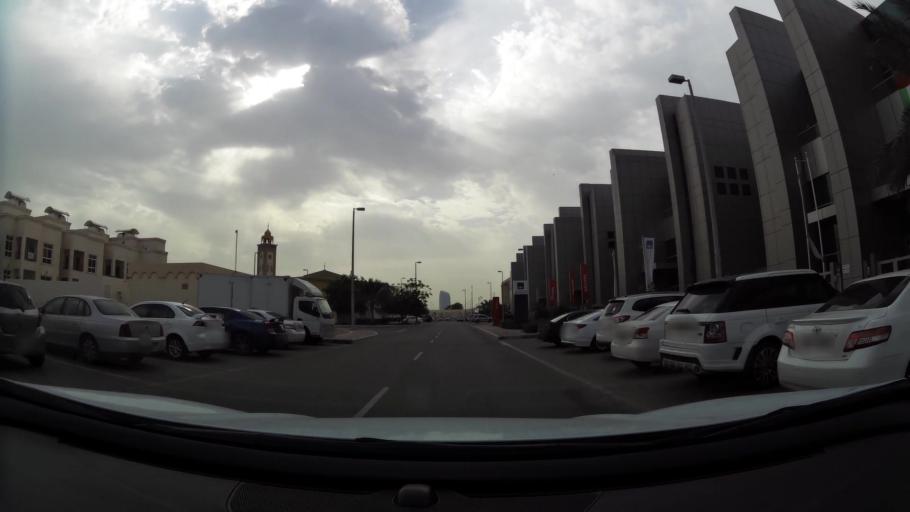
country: AE
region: Abu Dhabi
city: Abu Dhabi
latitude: 24.4721
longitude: 54.3855
